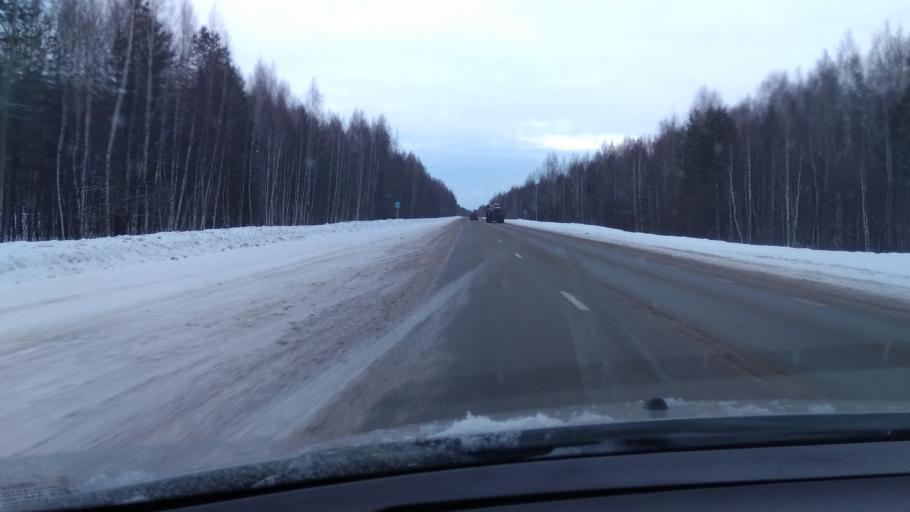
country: RU
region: Sverdlovsk
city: Tsementnyy
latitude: 57.4172
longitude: 60.2109
